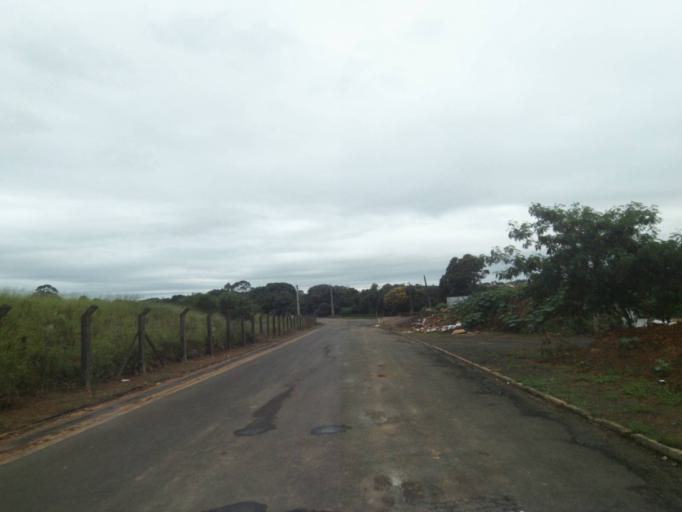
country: BR
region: Parana
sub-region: Telemaco Borba
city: Telemaco Borba
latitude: -24.3259
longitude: -50.6531
